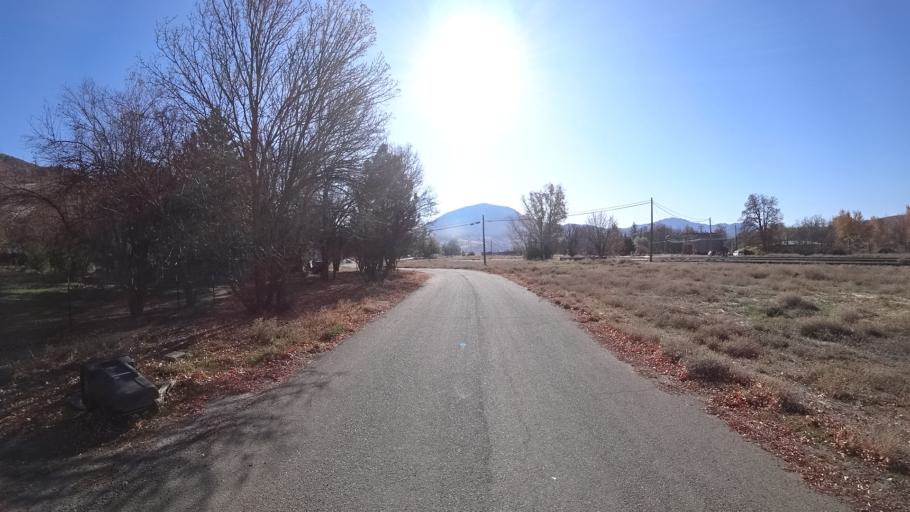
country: US
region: California
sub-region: Siskiyou County
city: Montague
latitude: 41.9116
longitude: -122.5560
